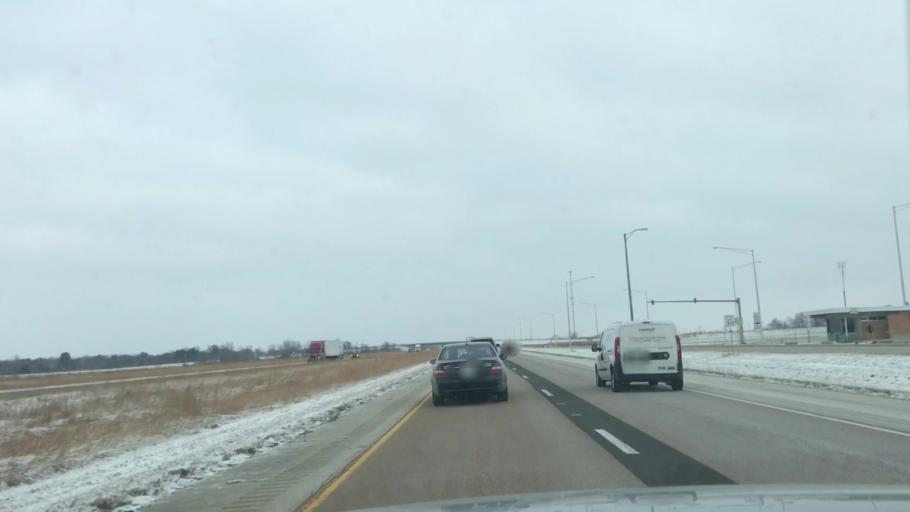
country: US
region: Illinois
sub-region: Montgomery County
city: Litchfield
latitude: 39.2269
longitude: -89.6443
